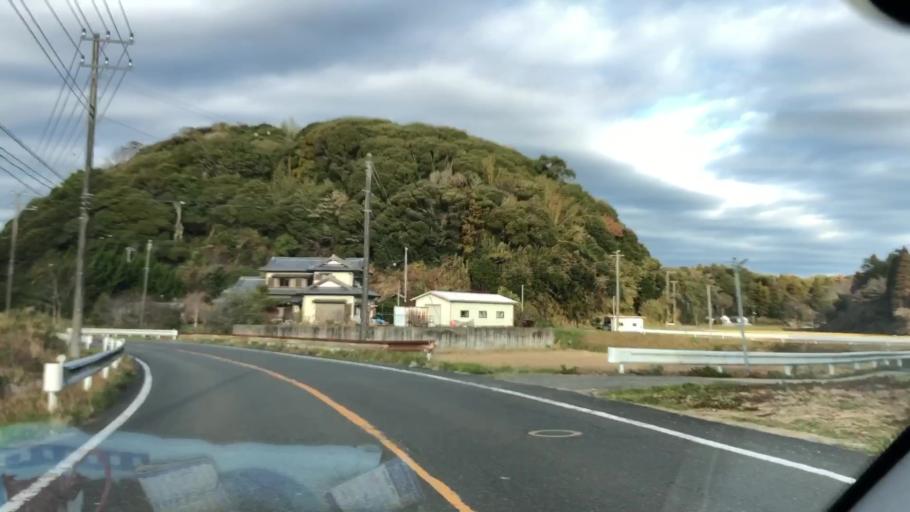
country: JP
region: Chiba
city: Tateyama
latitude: 34.9900
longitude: 139.9268
